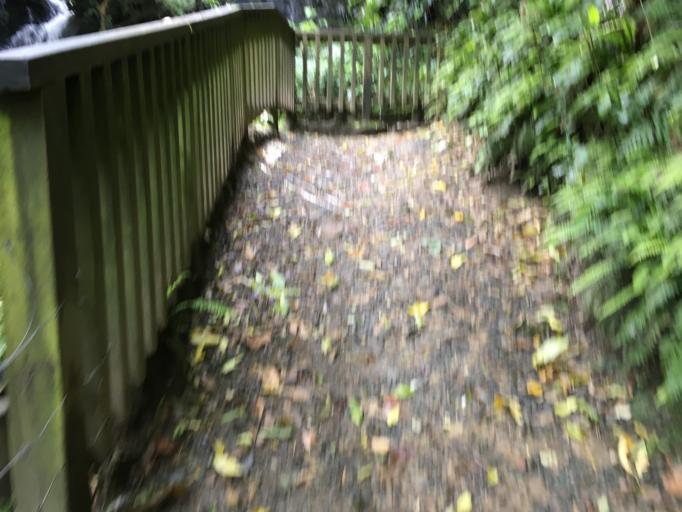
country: NZ
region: Otago
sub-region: Clutha District
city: Papatowai
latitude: -46.5033
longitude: 169.4886
